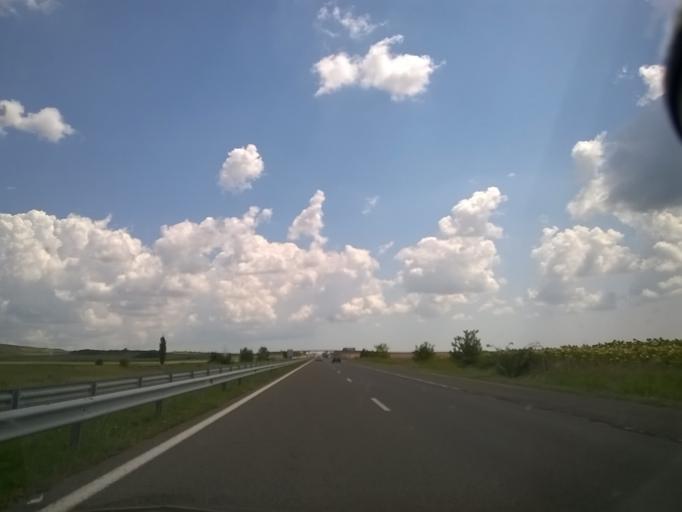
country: BG
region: Burgas
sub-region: Obshtina Kameno
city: Kameno
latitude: 42.6043
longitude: 27.3087
